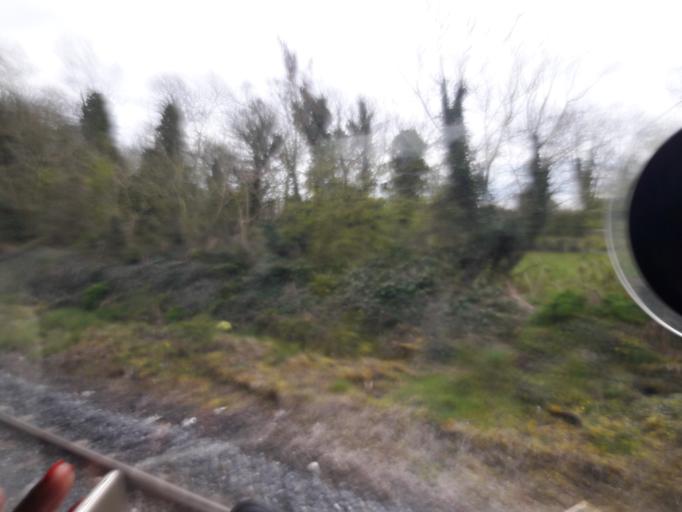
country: IE
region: Leinster
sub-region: An Longfort
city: Edgeworthstown
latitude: 53.6884
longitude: -7.6012
